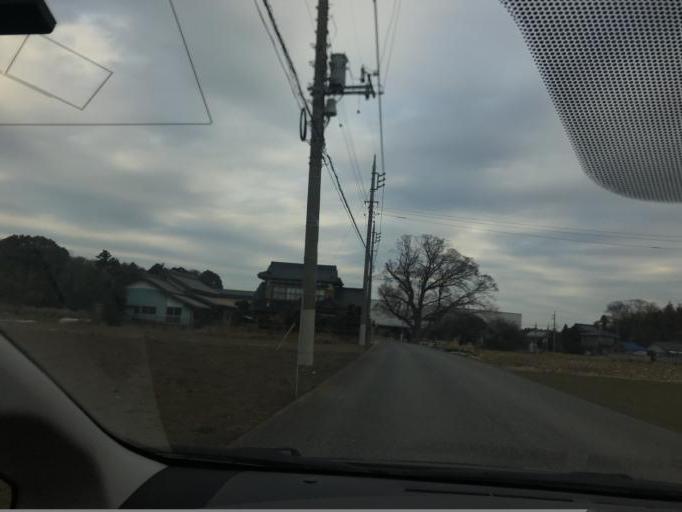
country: JP
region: Ibaraki
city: Mitsukaido
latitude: 36.0369
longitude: 140.0311
